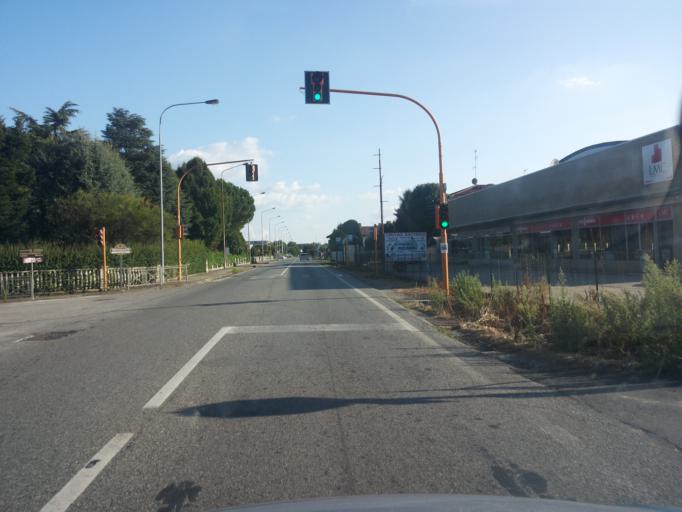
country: IT
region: Piedmont
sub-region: Provincia di Torino
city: Romano Canavese
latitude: 45.3968
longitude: 7.8840
